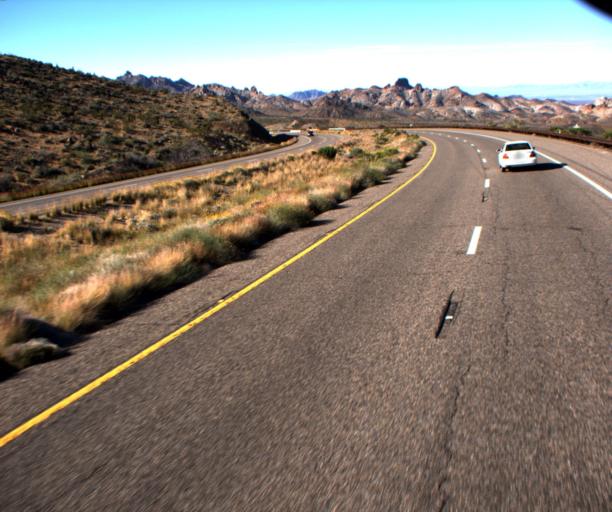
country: US
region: Nevada
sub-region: Clark County
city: Laughlin
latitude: 35.2094
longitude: -114.4027
